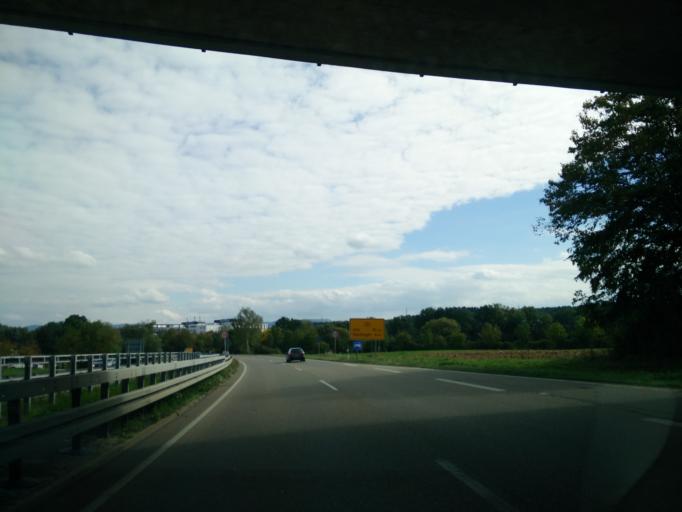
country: DE
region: Baden-Wuerttemberg
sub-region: Tuebingen Region
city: Kusterdingen
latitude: 48.4974
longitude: 9.1288
